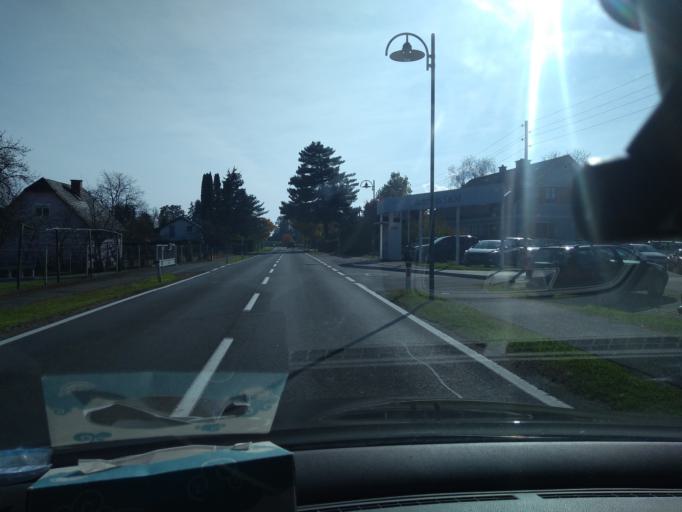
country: AT
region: Styria
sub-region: Politischer Bezirk Leibnitz
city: Kaindorf an der Sulm
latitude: 46.8270
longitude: 15.5439
